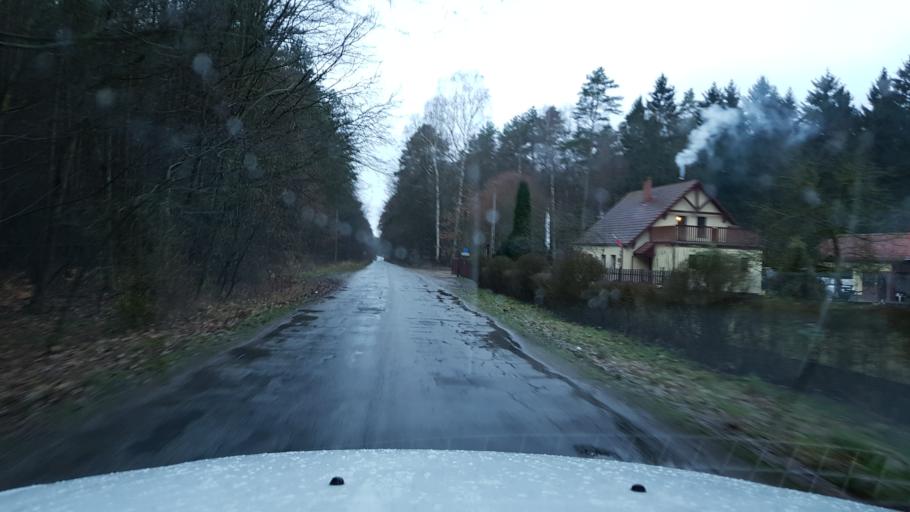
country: PL
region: West Pomeranian Voivodeship
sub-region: Powiat goleniowski
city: Mosty
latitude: 53.5586
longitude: 14.9875
